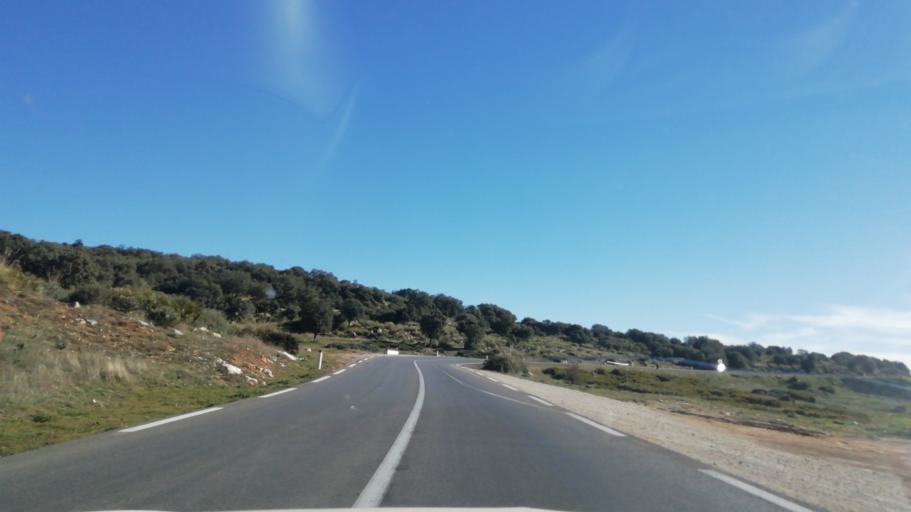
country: DZ
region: Tlemcen
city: Mansoura
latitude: 34.8283
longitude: -1.3699
